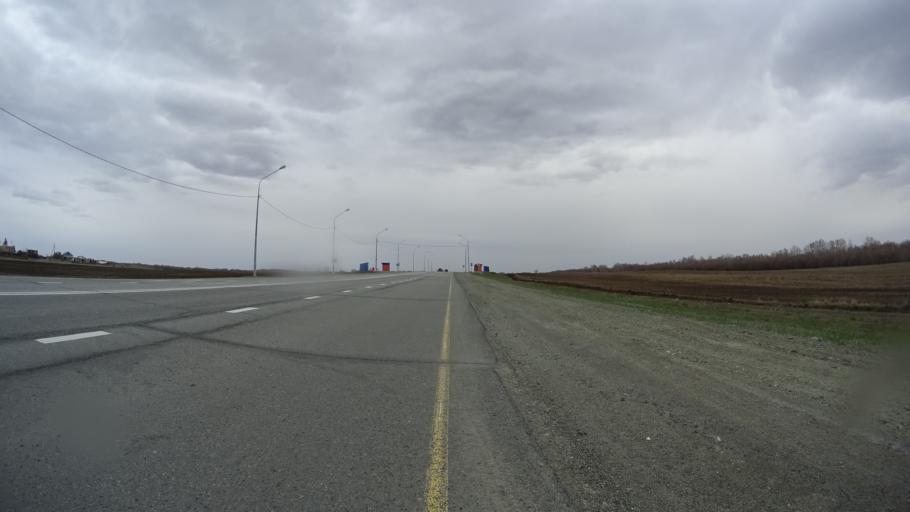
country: RU
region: Chelyabinsk
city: Krasnogorskiy
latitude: 54.6732
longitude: 61.2494
